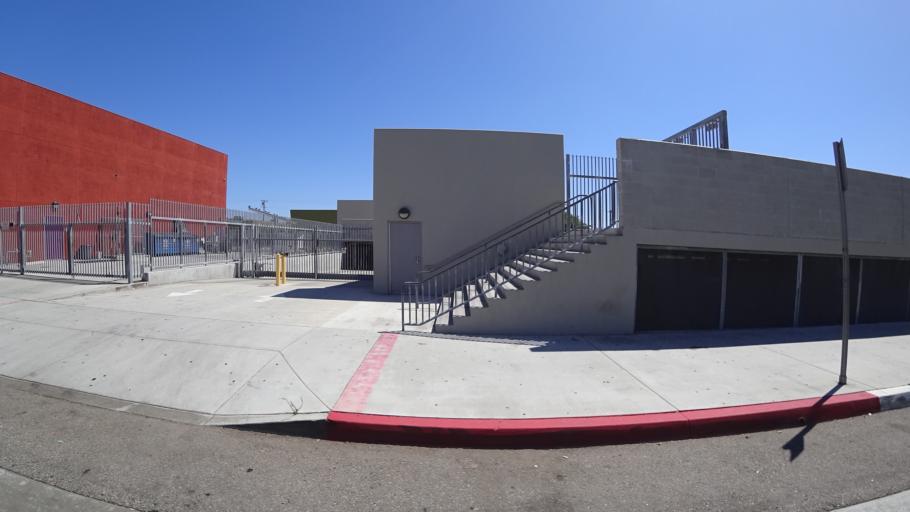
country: US
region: California
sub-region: Los Angeles County
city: Lennox
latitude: 33.9418
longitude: -118.3469
